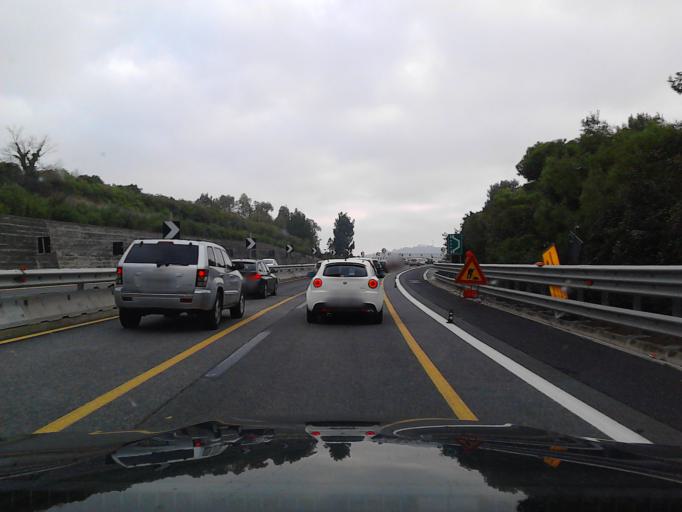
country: IT
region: Abruzzo
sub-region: Provincia di Teramo
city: Tortoreto Lido
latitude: 42.7864
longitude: 13.9355
